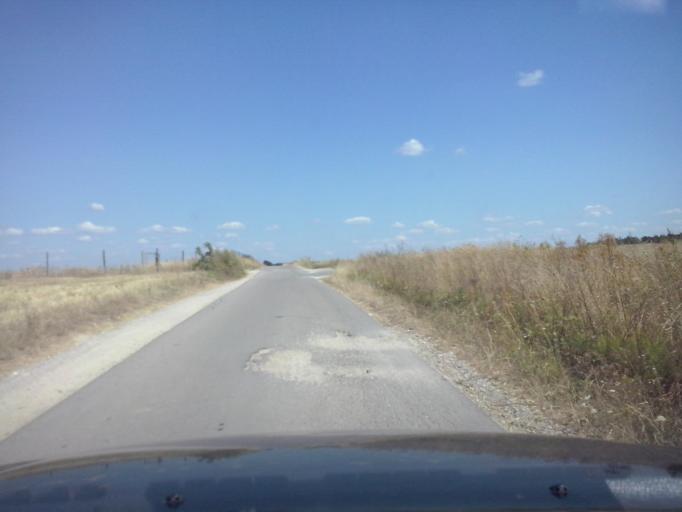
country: PL
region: Swietokrzyskie
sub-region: Powiat buski
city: Gnojno
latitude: 50.5930
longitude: 20.8949
